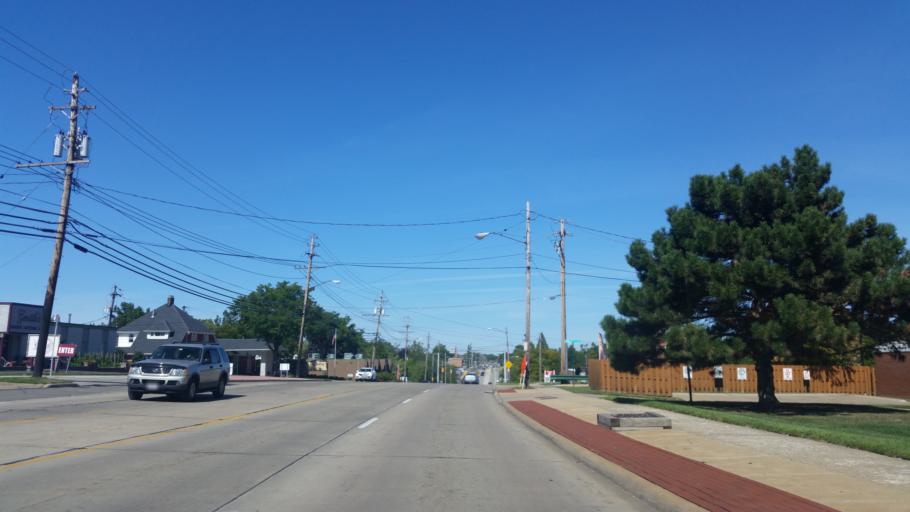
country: US
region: Ohio
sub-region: Cuyahoga County
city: Brooklyn Heights
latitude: 41.4086
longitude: -81.6920
